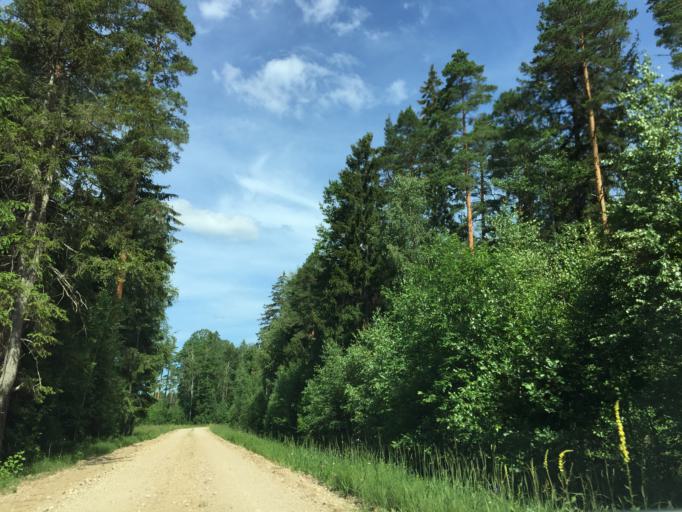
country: LV
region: Dundaga
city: Dundaga
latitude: 57.4252
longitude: 22.0755
